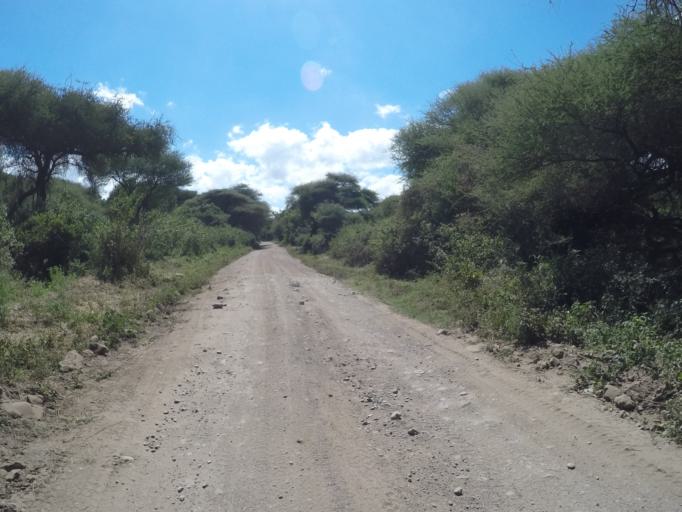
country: TZ
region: Arusha
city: Mto wa Mbu
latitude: -3.4159
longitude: 35.8094
